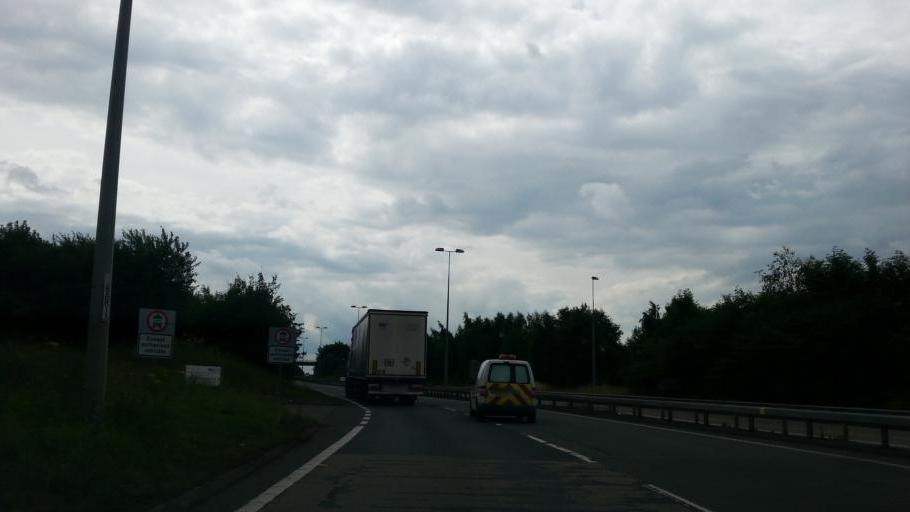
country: GB
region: England
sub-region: Warwickshire
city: Curdworth
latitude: 52.5664
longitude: -1.7698
